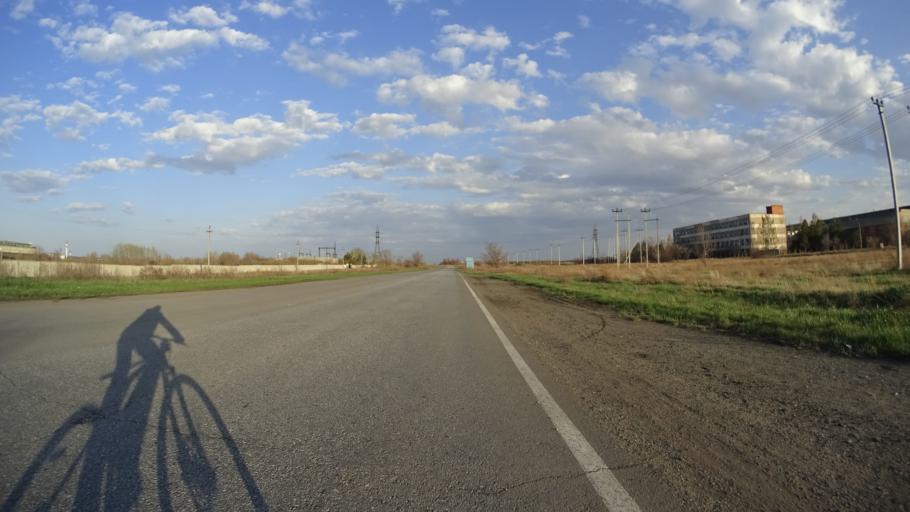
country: RU
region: Chelyabinsk
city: Troitsk
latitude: 54.0647
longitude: 61.5687
